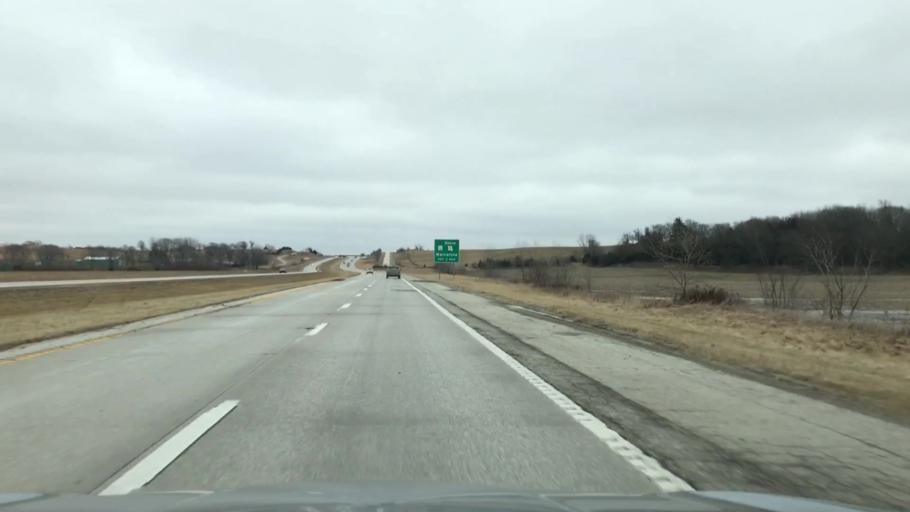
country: US
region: Missouri
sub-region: Linn County
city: Marceline
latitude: 39.7609
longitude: -92.9669
